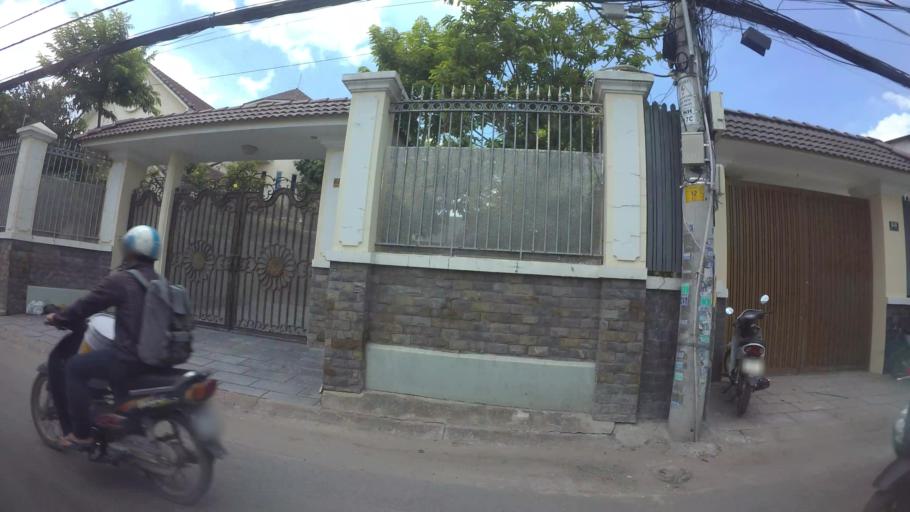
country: VN
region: Ho Chi Minh City
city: Quan Chin
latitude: 10.8237
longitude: 106.7611
